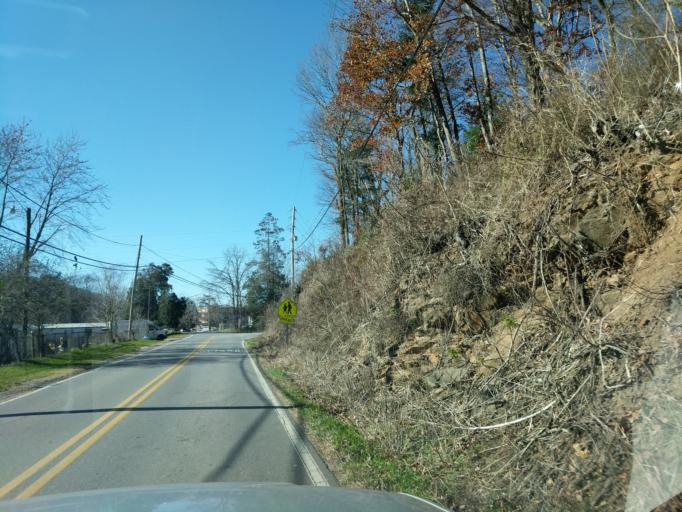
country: US
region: North Carolina
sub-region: Buncombe County
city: Swannanoa
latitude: 35.6022
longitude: -82.4012
